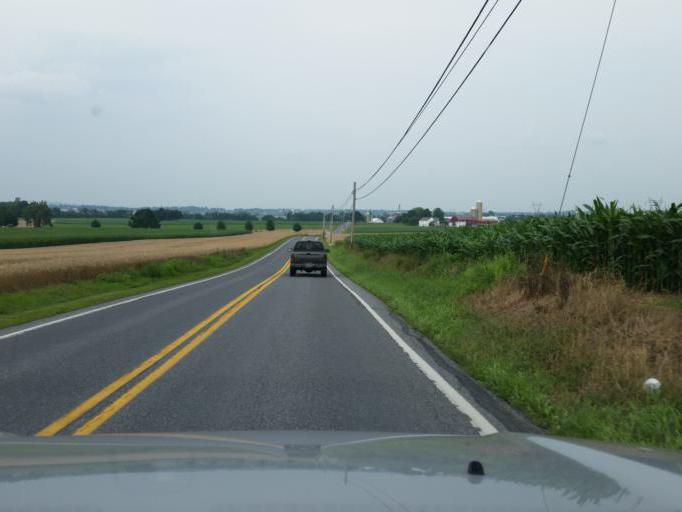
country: US
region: Pennsylvania
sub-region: Lancaster County
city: Manheim
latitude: 40.1563
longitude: -76.3634
